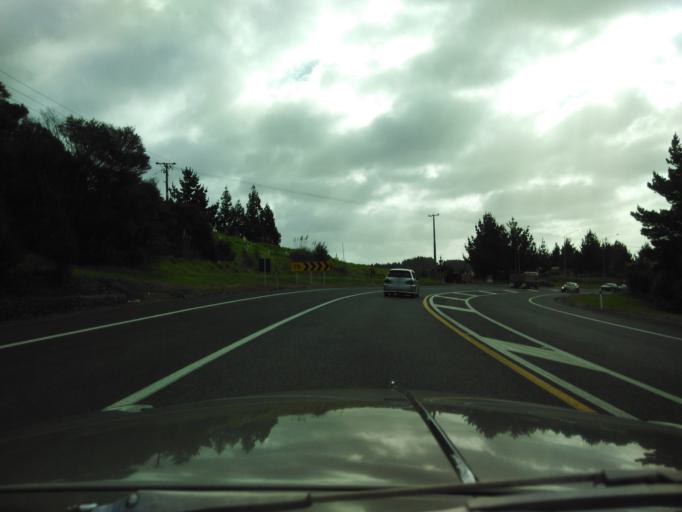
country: NZ
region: Auckland
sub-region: Auckland
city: Warkworth
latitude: -36.4705
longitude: 174.6477
